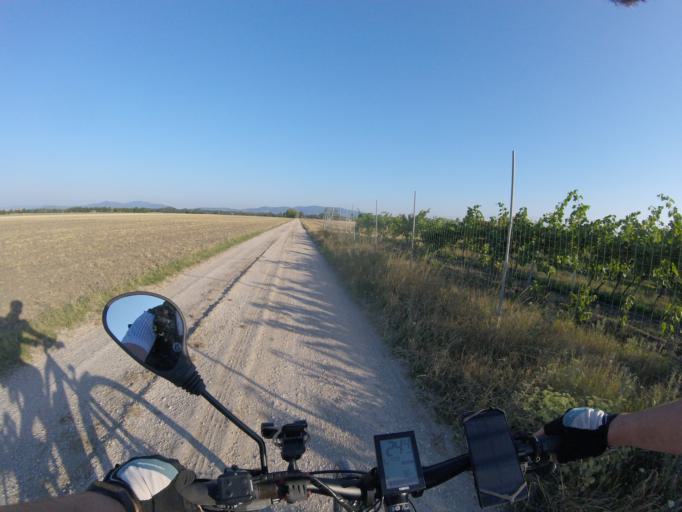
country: AT
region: Lower Austria
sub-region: Politischer Bezirk Baden
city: Trumau
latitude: 47.9842
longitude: 16.3519
